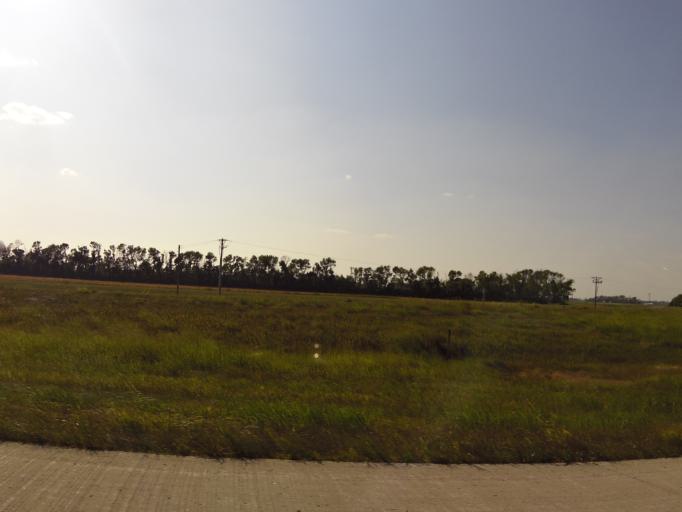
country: US
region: North Dakota
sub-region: Walsh County
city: Grafton
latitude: 48.2937
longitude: -97.1893
